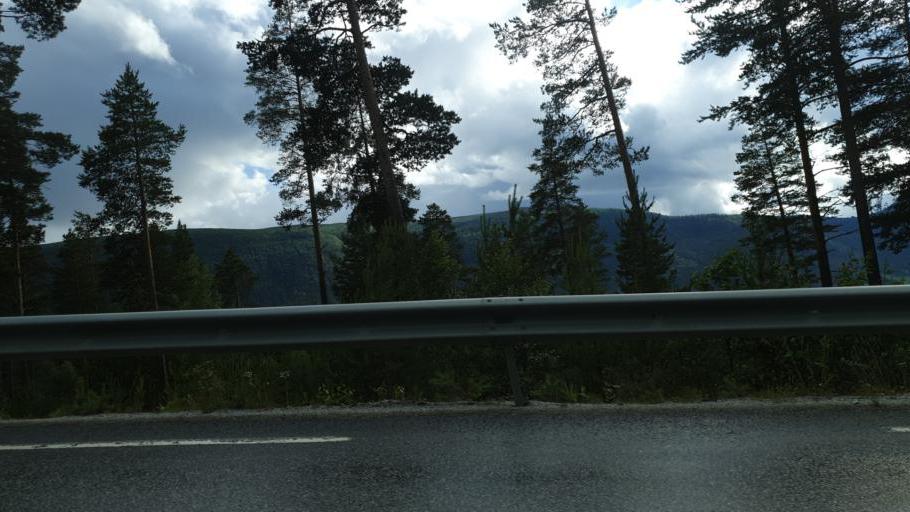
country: NO
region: Oppland
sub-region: Dovre
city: Dovre
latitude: 61.8597
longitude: 9.2350
